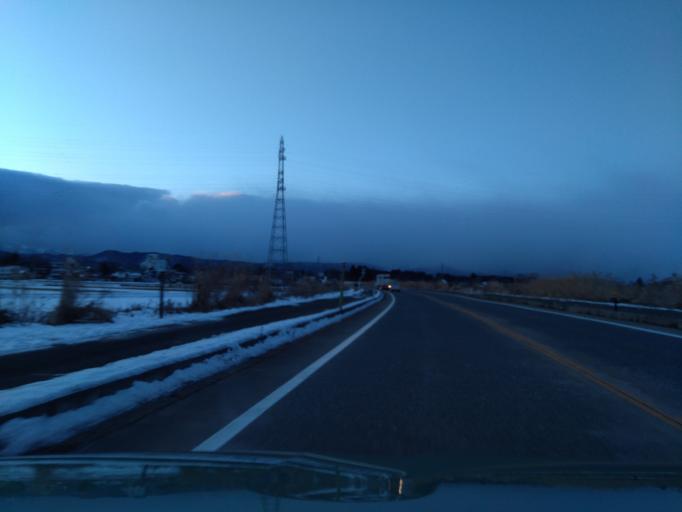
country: JP
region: Iwate
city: Shizukuishi
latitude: 39.7014
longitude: 140.9744
